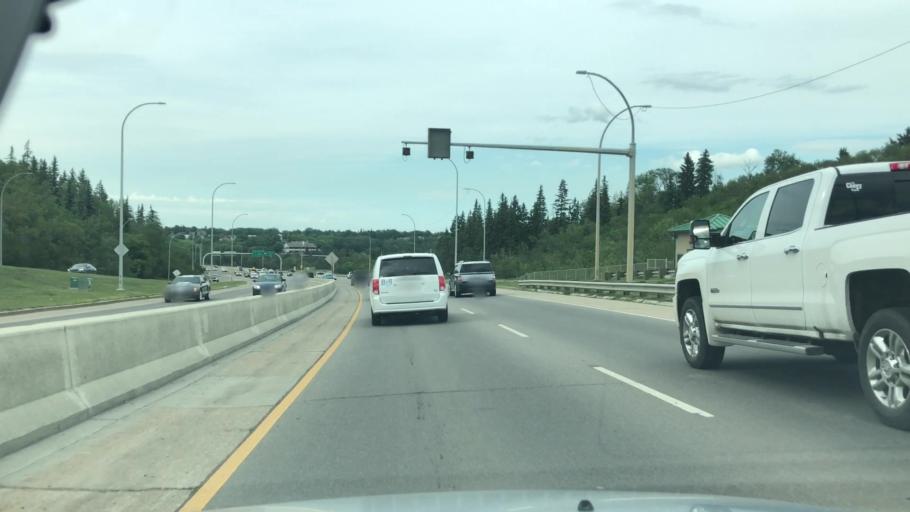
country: CA
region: Alberta
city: Edmonton
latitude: 53.5510
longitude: -113.4378
